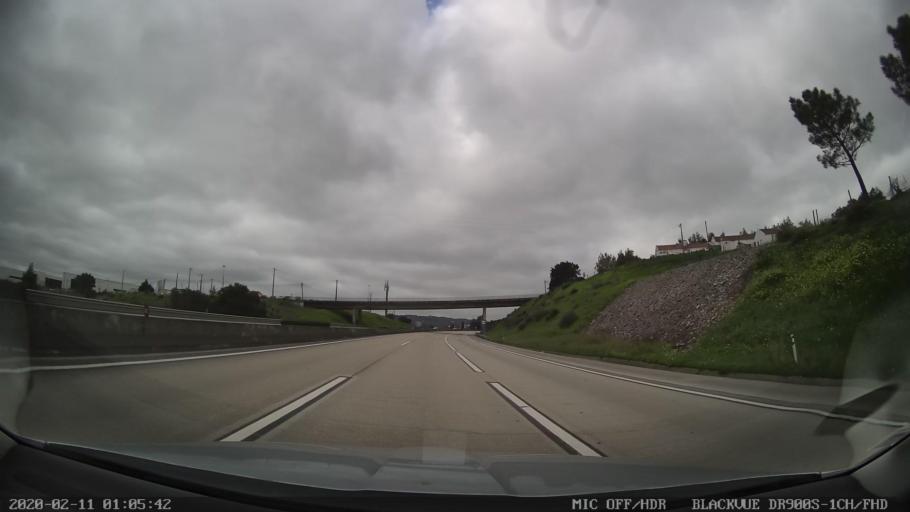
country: PT
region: Lisbon
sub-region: Loures
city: Santo Antao do Tojal
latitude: 38.8619
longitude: -9.1556
